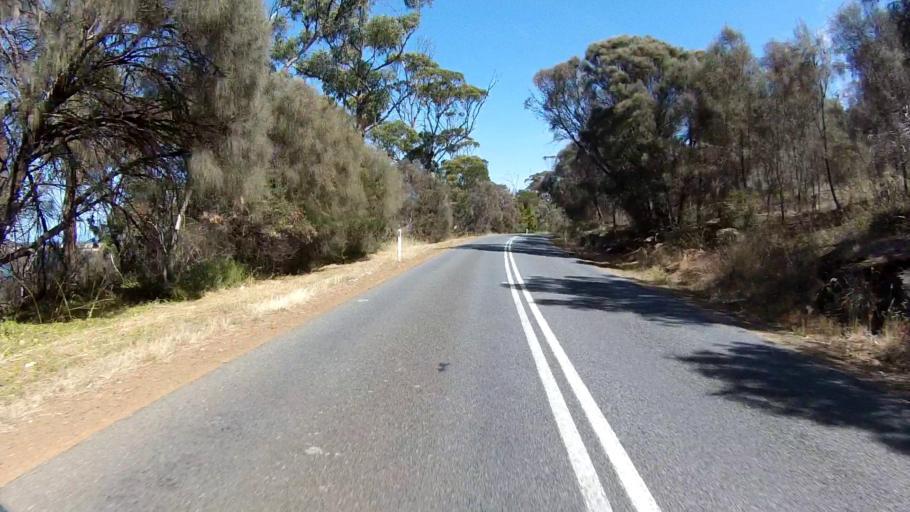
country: AU
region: Tasmania
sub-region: Sorell
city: Sorell
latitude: -42.2362
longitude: 148.0160
